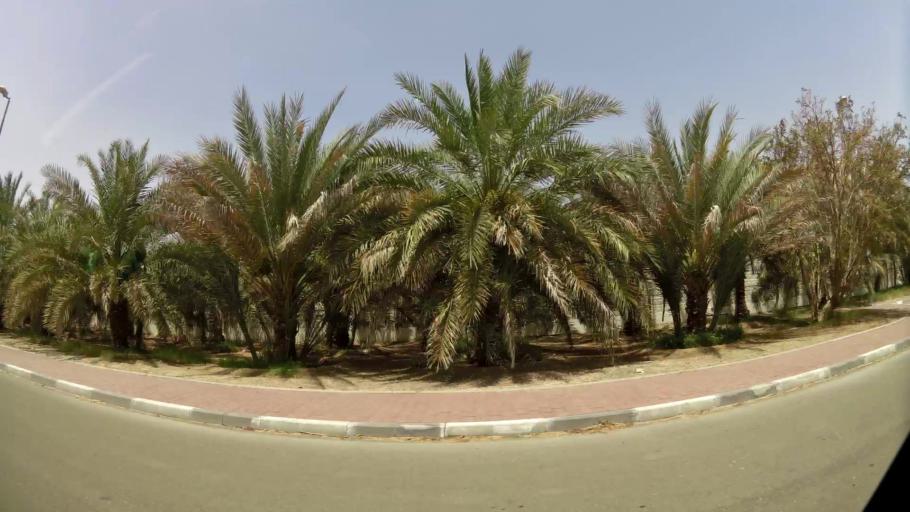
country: AE
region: Abu Dhabi
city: Al Ain
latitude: 24.1989
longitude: 55.7057
